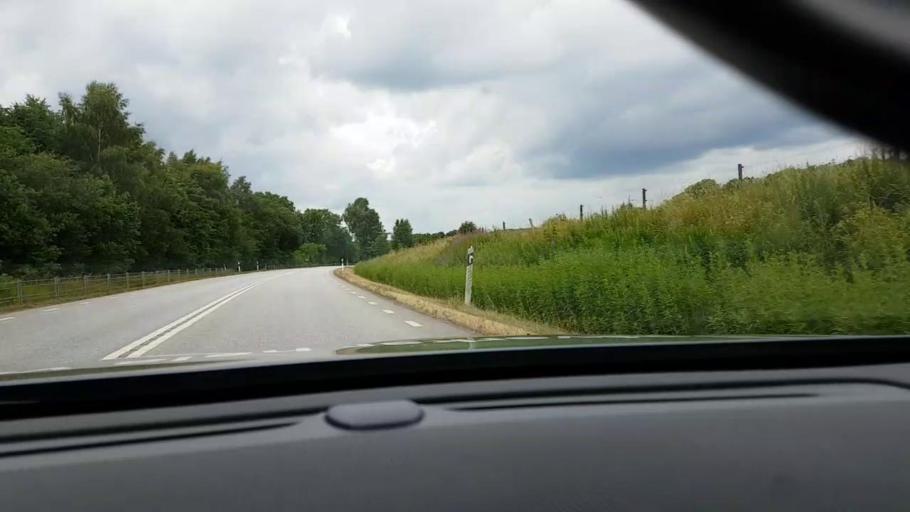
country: SE
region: Skane
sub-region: Horby Kommun
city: Hoerby
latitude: 55.8747
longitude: 13.6323
